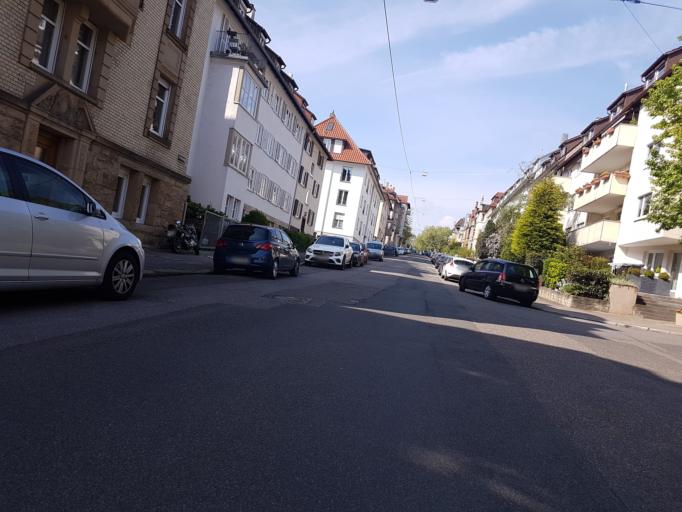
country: DE
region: Baden-Wuerttemberg
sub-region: Regierungsbezirk Stuttgart
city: Stuttgart-Ost
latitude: 48.7871
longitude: 9.2004
